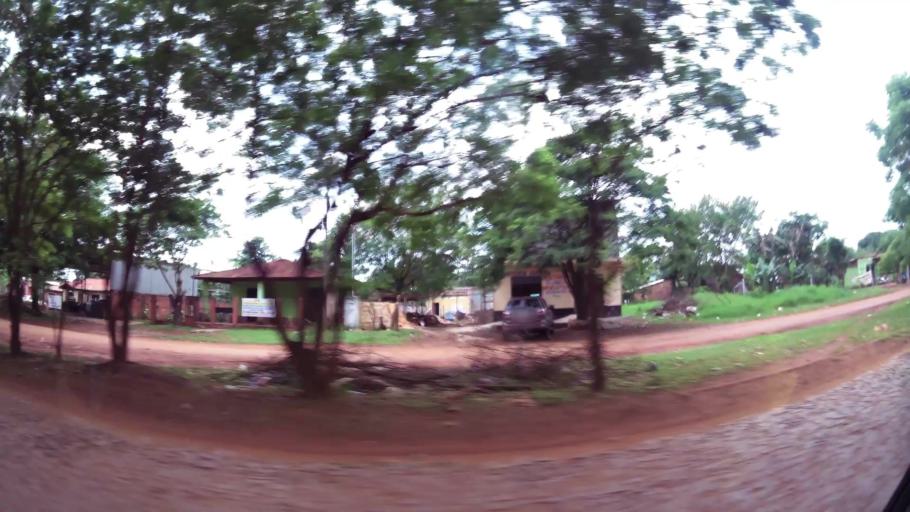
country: PY
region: Alto Parana
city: Presidente Franco
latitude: -25.5385
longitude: -54.6507
